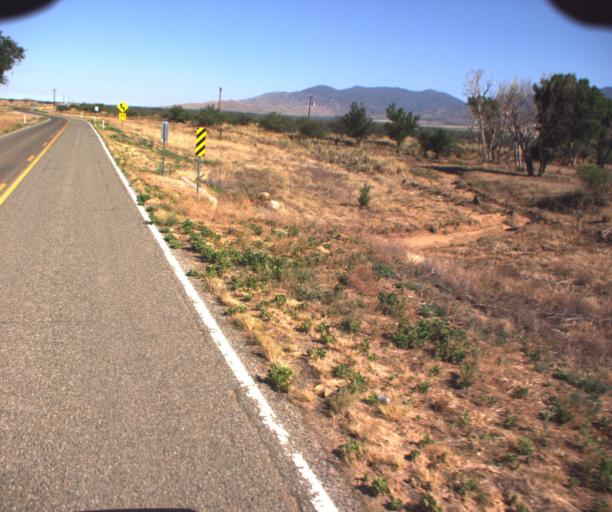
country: US
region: Arizona
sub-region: Graham County
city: Swift Trail Junction
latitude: 32.5891
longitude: -109.9679
